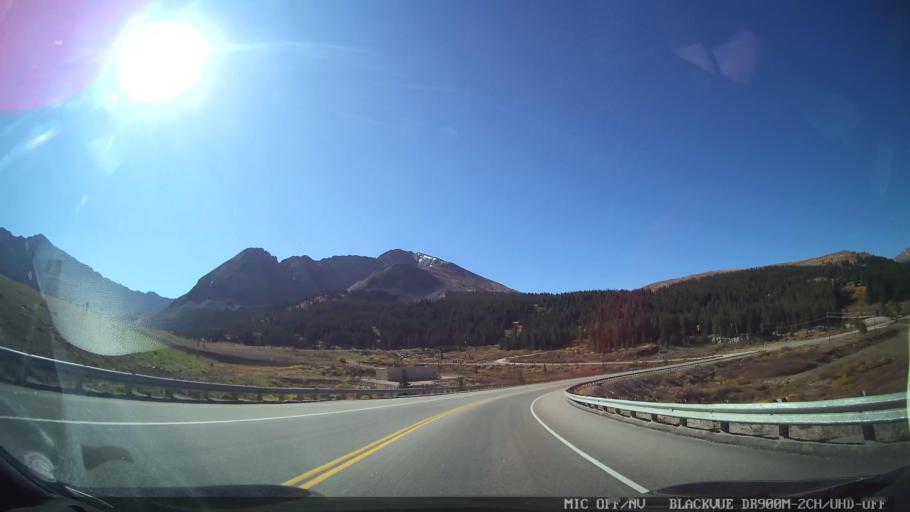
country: US
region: Colorado
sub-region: Lake County
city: Leadville
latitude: 39.3612
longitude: -106.1748
